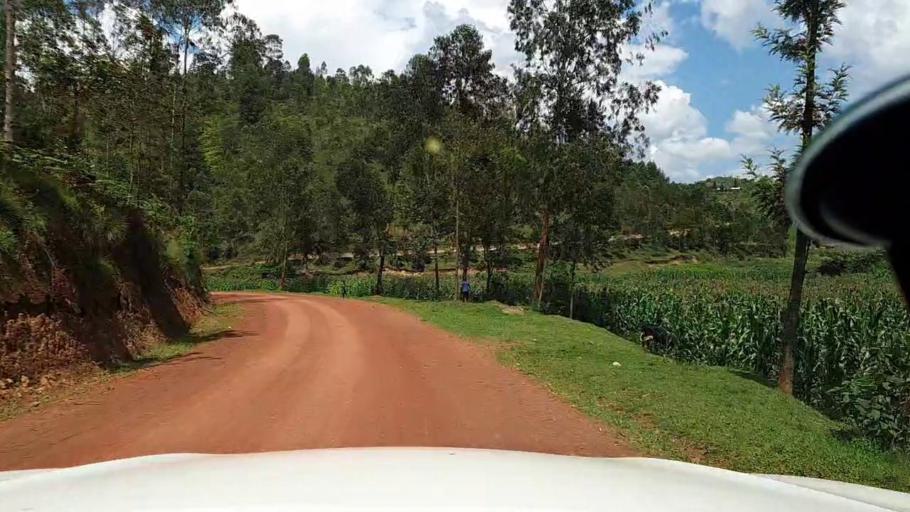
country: RW
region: Northern Province
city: Byumba
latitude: -1.7003
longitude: 29.8360
